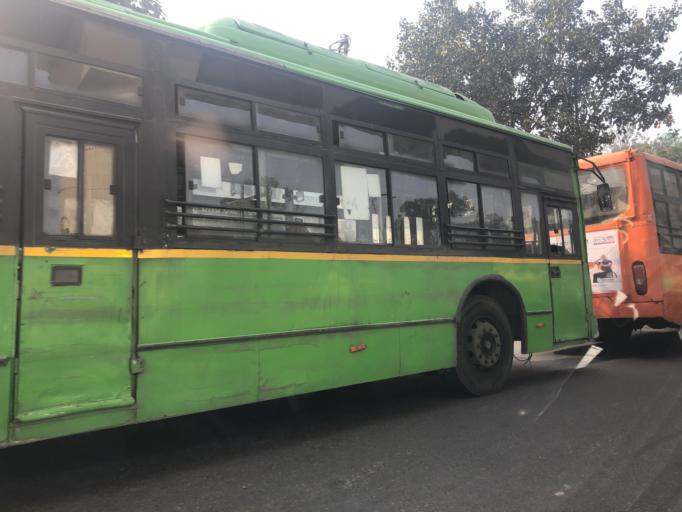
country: IN
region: NCT
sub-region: North West Delhi
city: Pitampura
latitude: 28.6749
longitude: 77.1298
